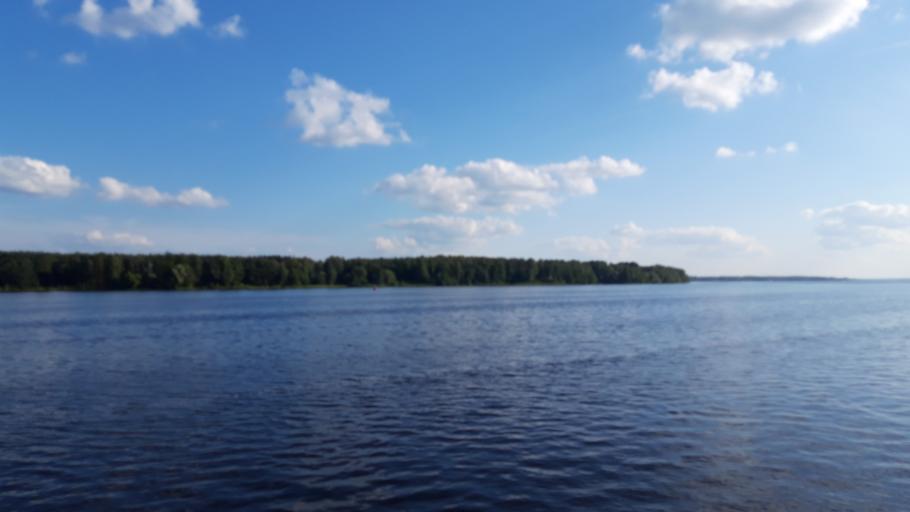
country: RU
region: Tverskaya
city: Konakovo
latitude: 56.6989
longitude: 36.7065
